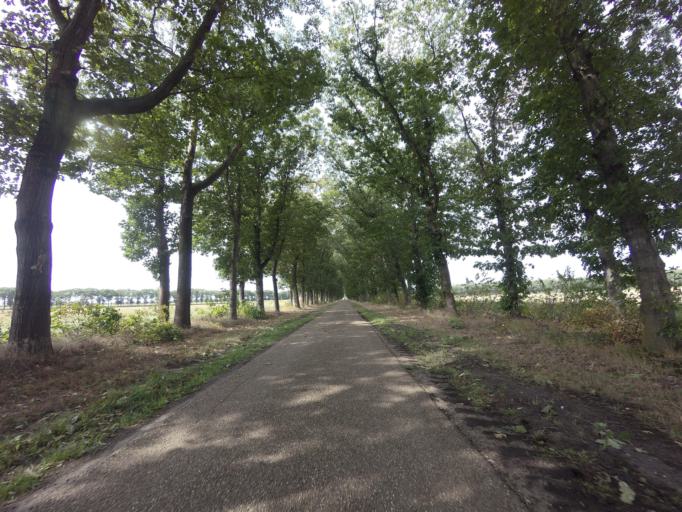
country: NL
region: North Brabant
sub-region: Gemeente Sint Anthonis
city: Sint Anthonis
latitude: 51.5556
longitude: 5.8320
